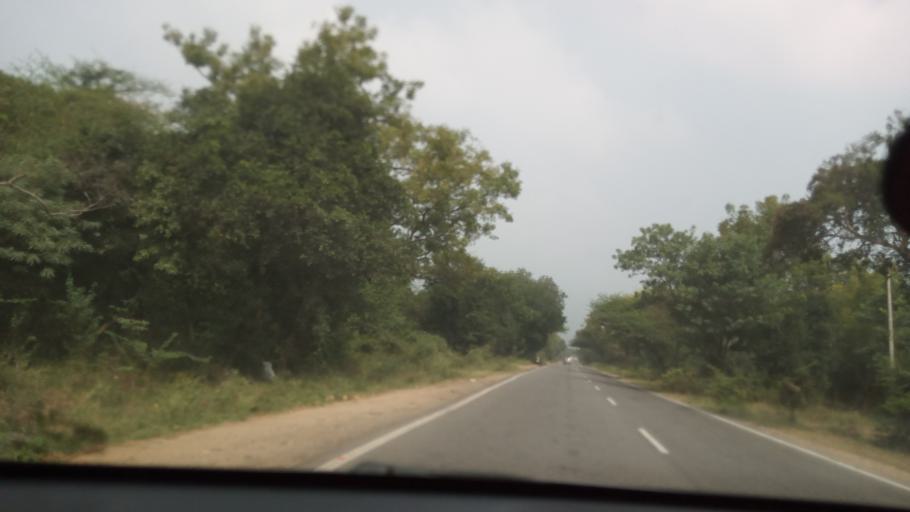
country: IN
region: Tamil Nadu
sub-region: Erode
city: Sathyamangalam
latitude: 11.5593
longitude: 77.1365
